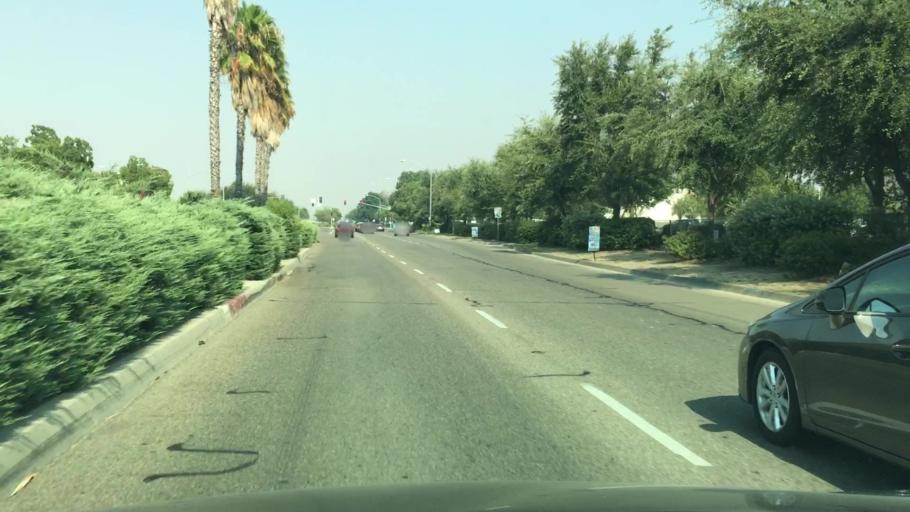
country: US
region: California
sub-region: Fresno County
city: West Park
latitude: 36.8370
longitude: -119.8814
